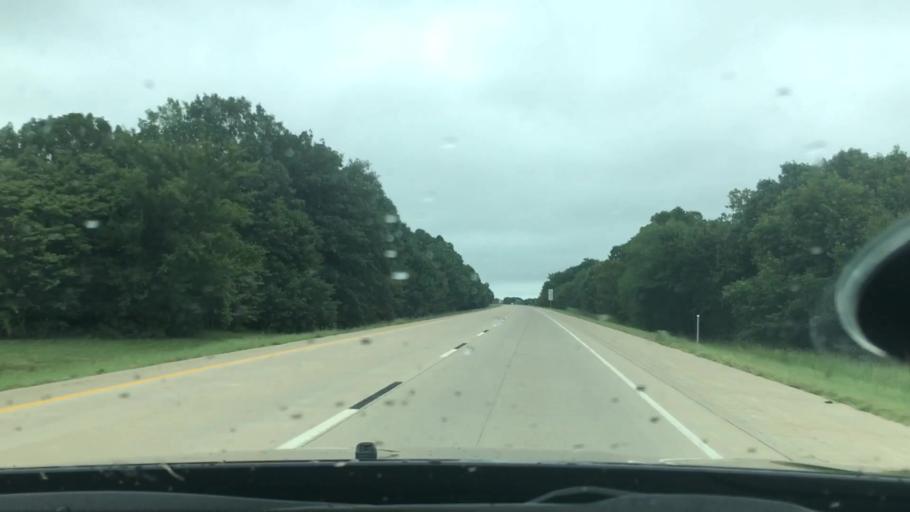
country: US
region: Oklahoma
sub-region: McIntosh County
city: Checotah
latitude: 35.4517
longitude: -95.7069
